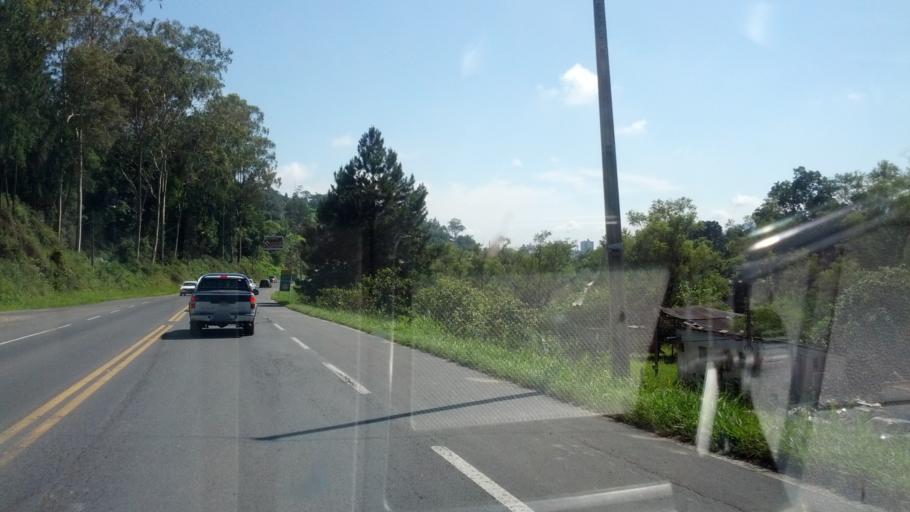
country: BR
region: Santa Catarina
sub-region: Rio Do Sul
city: Rio do Sul
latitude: -27.2241
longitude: -49.6645
